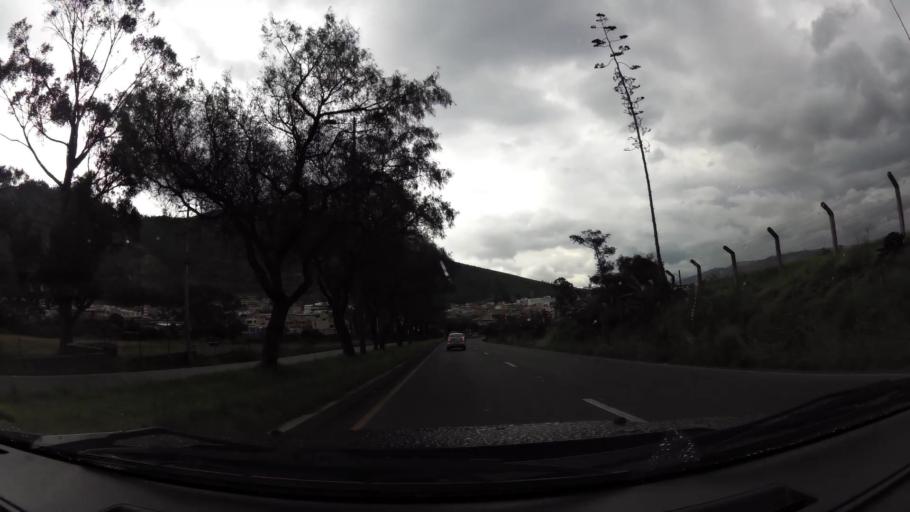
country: EC
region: Pichincha
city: Quito
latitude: -0.0768
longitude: -78.4805
